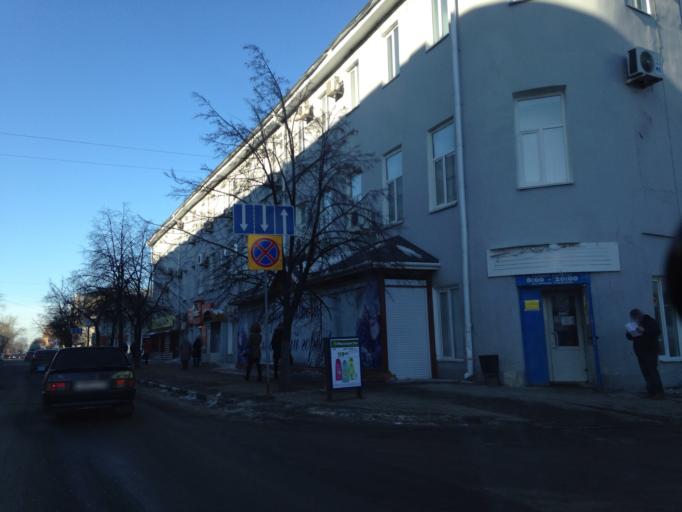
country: RU
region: Ulyanovsk
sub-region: Ulyanovskiy Rayon
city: Ulyanovsk
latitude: 54.3197
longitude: 48.3950
